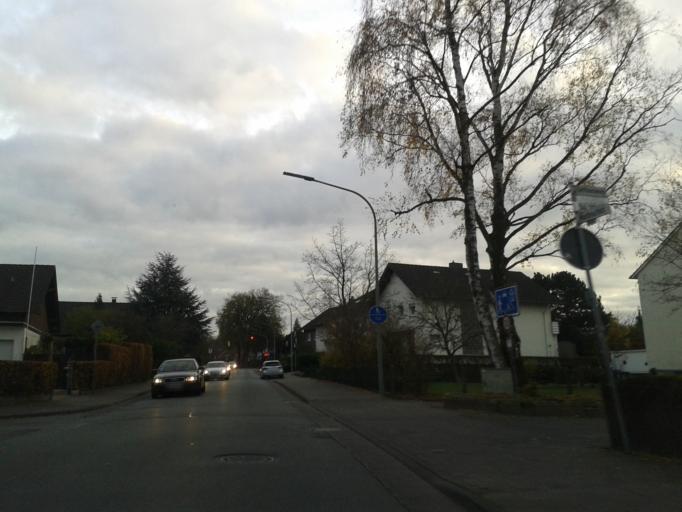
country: DE
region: North Rhine-Westphalia
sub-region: Regierungsbezirk Detmold
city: Paderborn
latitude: 51.7562
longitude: 8.7326
